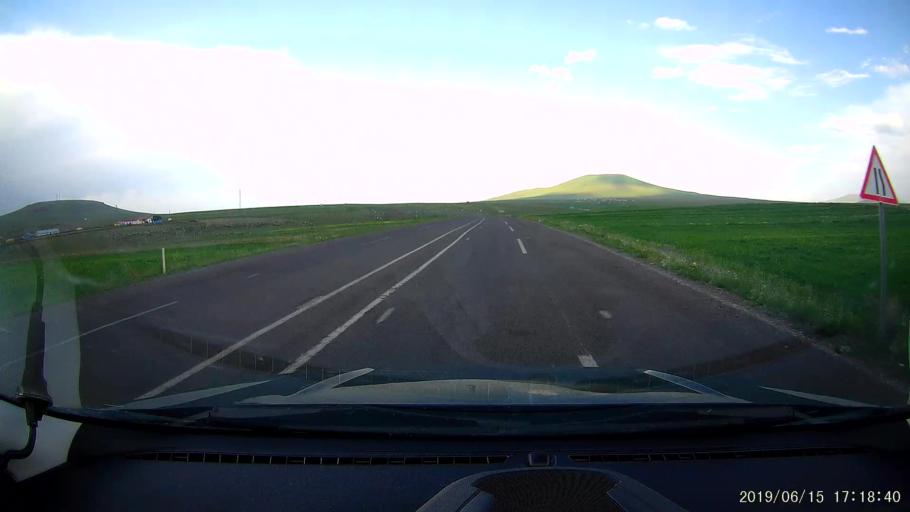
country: TR
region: Kars
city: Kars
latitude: 40.6131
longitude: 43.2629
